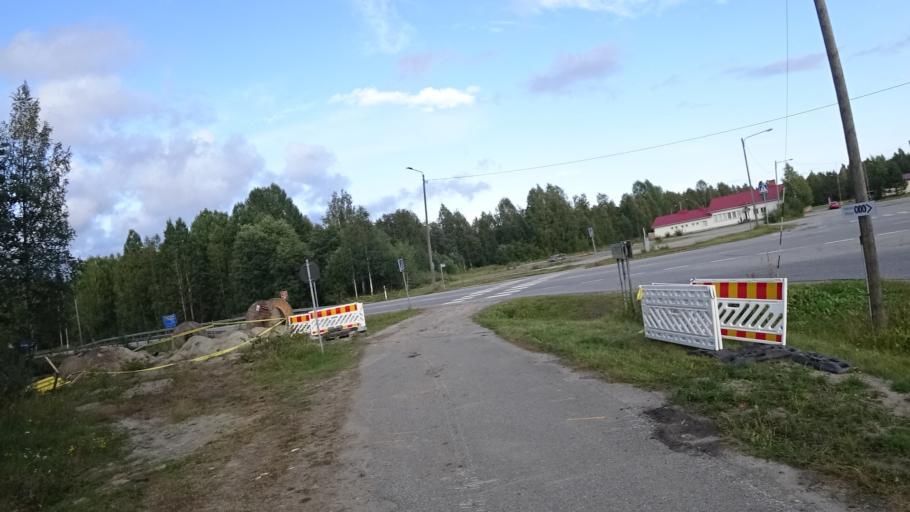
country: FI
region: North Karelia
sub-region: Joensuu
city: Ilomantsi
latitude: 62.6722
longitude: 30.9464
